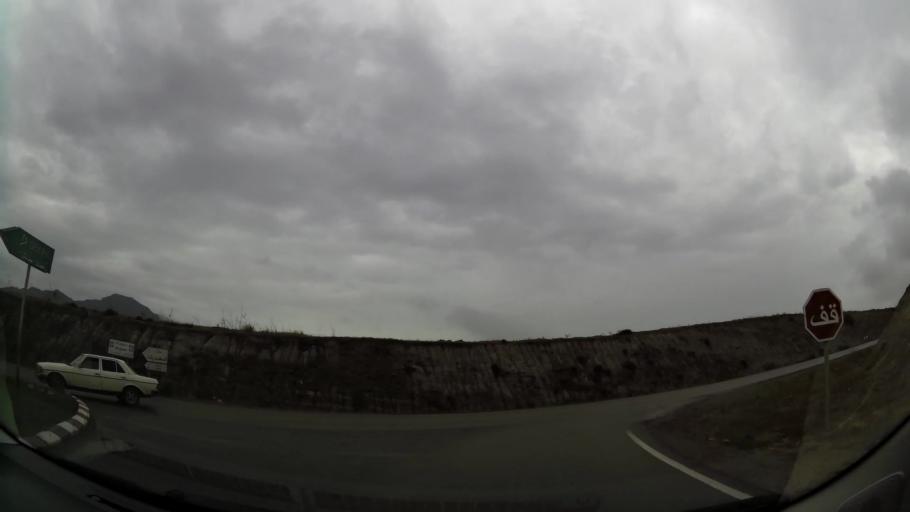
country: MA
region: Oriental
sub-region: Nador
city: Nador
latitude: 35.1494
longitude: -3.0189
